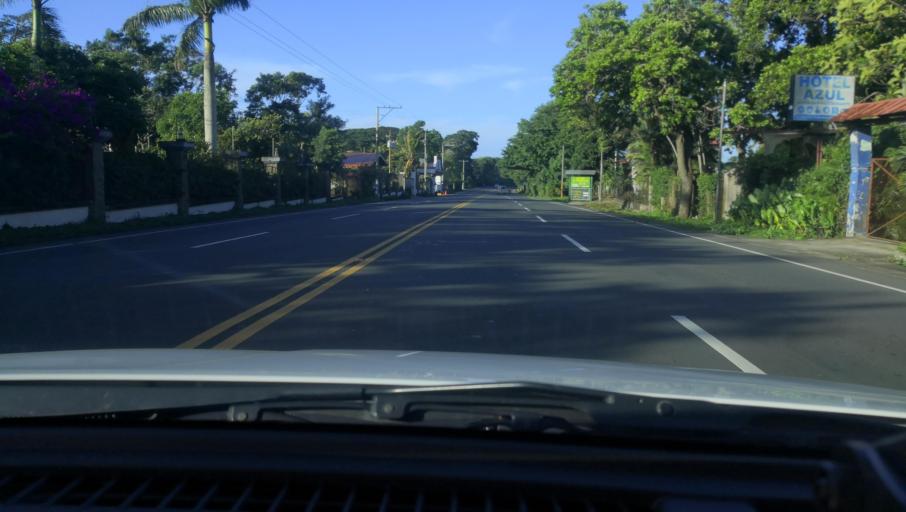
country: NI
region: Carazo
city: Diriamba
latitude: 11.8828
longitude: -86.2356
